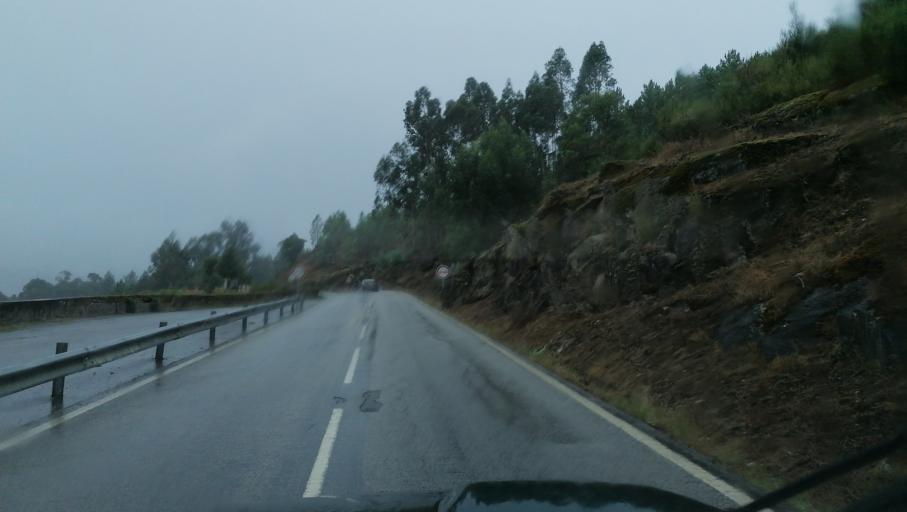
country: PT
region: Braga
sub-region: Cabeceiras de Basto
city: Cabeceiras de Basto
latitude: 41.5002
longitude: -7.8979
